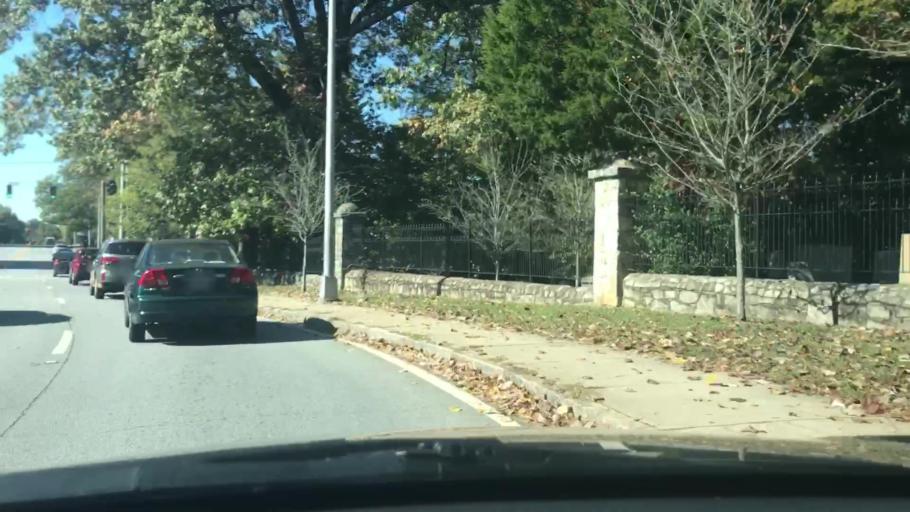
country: US
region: Georgia
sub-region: DeKalb County
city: Decatur
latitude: 33.7778
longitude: -84.2919
